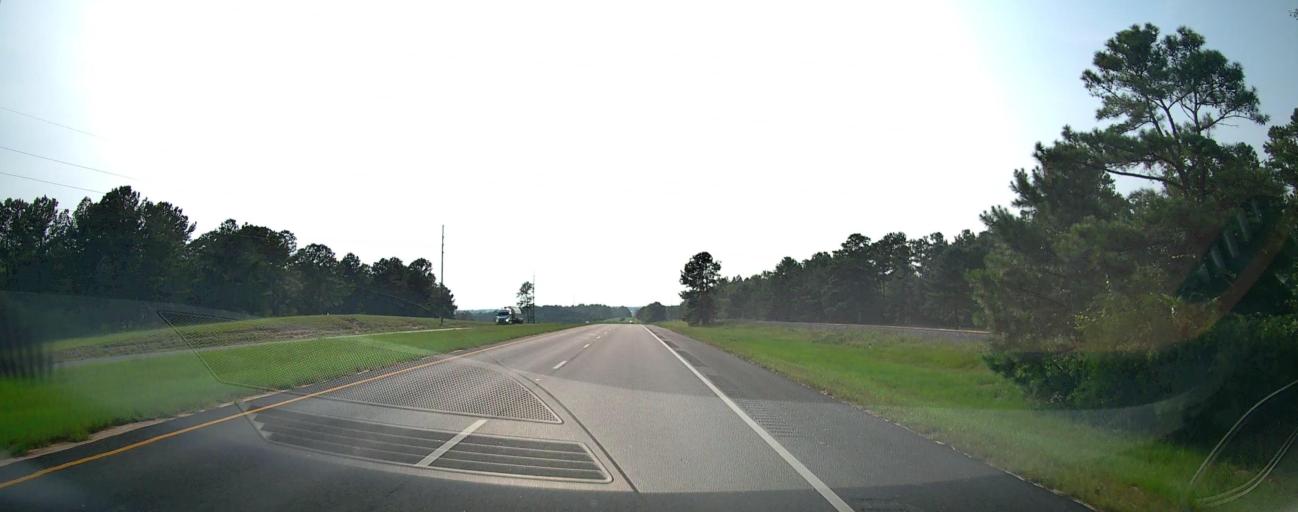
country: US
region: Georgia
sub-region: Taylor County
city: Butler
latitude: 32.5872
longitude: -84.3480
